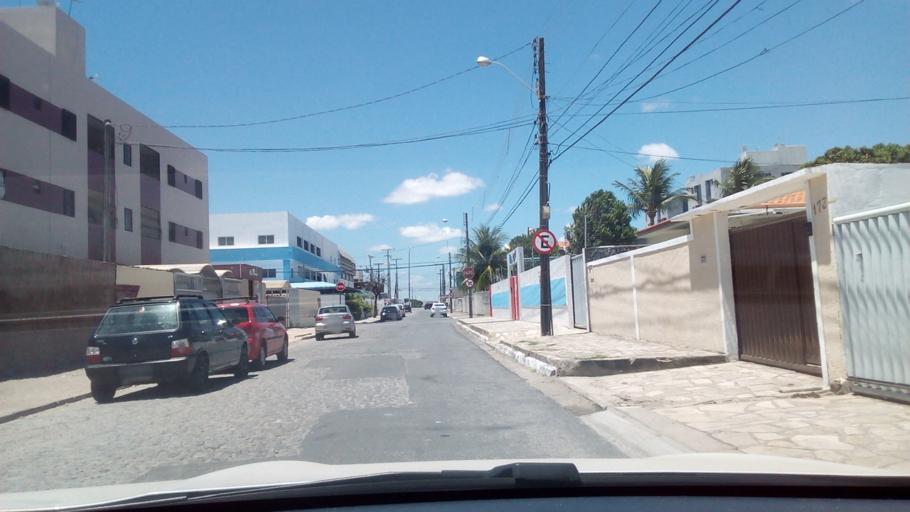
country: BR
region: Paraiba
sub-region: Joao Pessoa
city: Joao Pessoa
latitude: -7.1589
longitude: -34.8366
